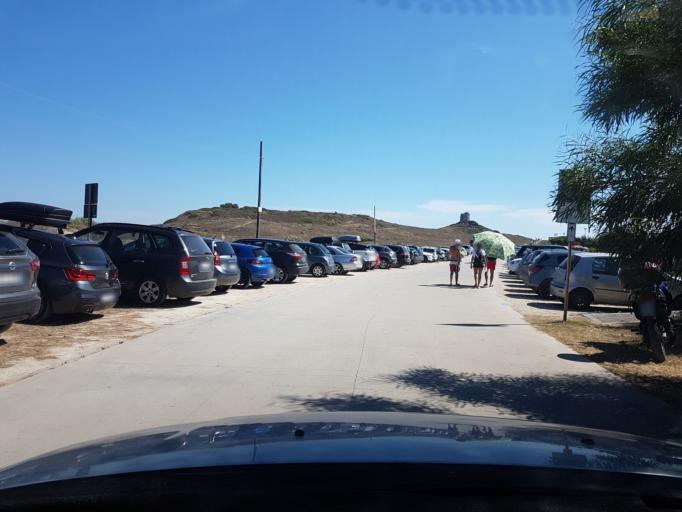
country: IT
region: Sardinia
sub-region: Provincia di Oristano
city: Cabras
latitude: 39.8805
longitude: 8.4395
